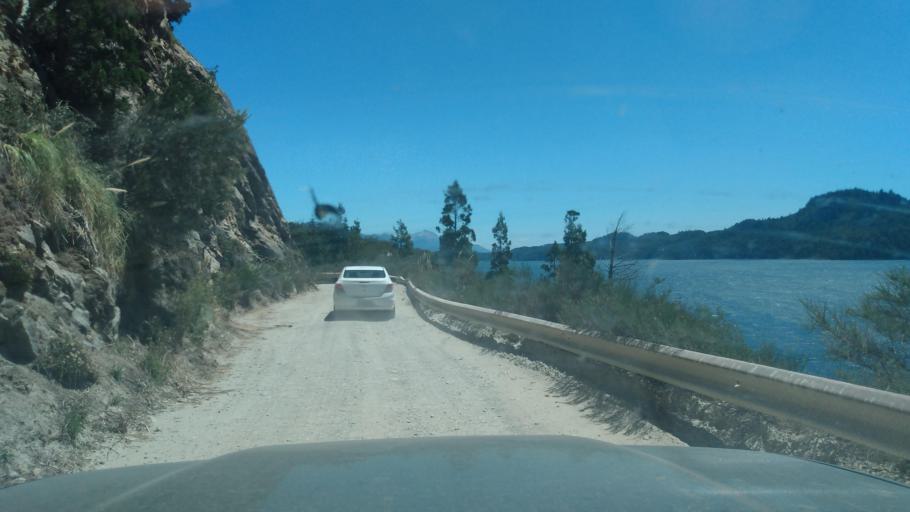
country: AR
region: Rio Negro
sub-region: Departamento de Bariloche
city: San Carlos de Bariloche
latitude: -41.1073
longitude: -71.4812
